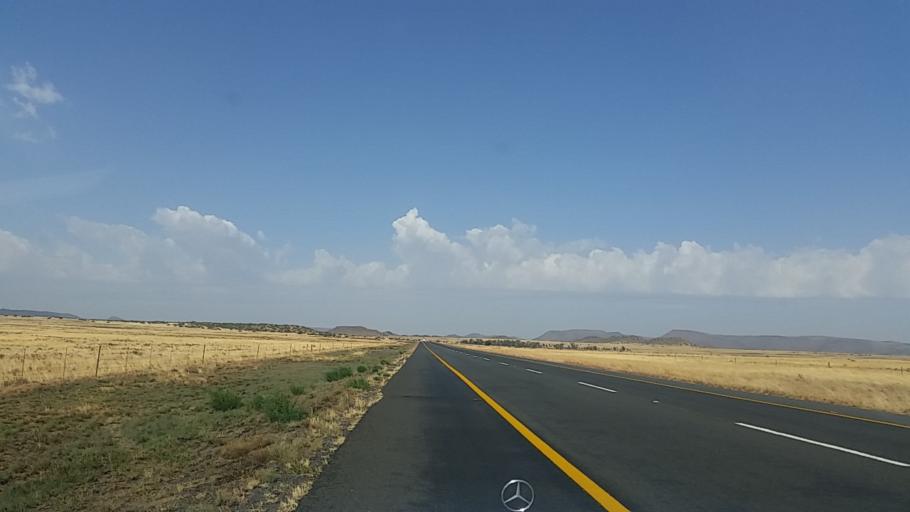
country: ZA
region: Orange Free State
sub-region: Xhariep District Municipality
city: Trompsburg
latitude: -30.4162
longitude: 25.6503
